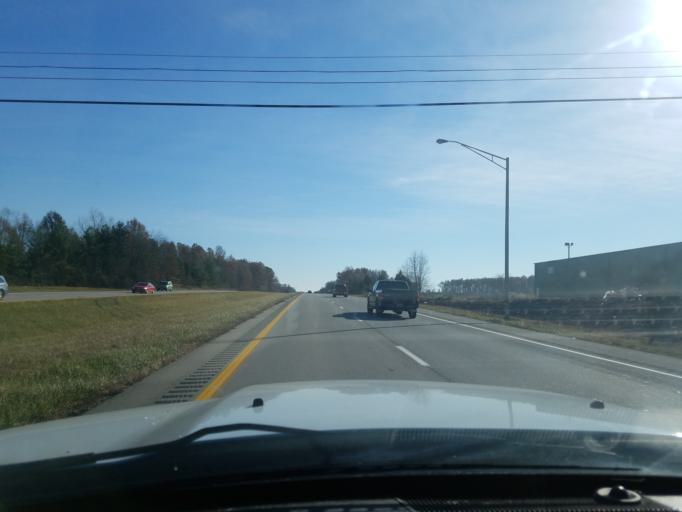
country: US
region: Ohio
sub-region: Brown County
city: Mount Orab
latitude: 39.0401
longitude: -83.9157
